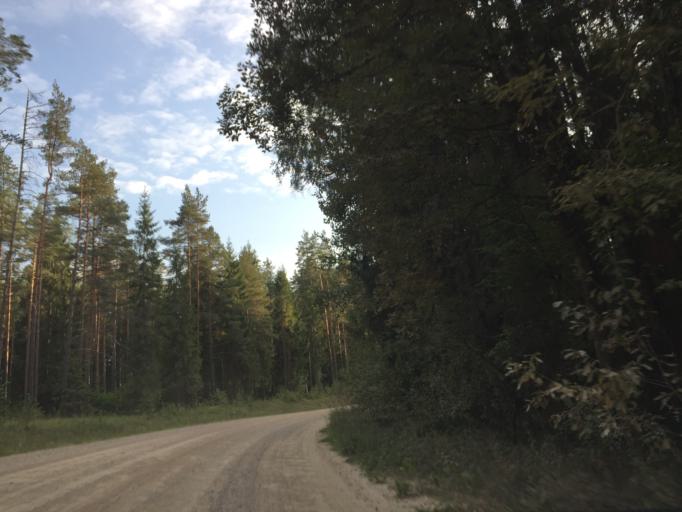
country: LV
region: Baldone
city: Baldone
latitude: 56.7875
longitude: 24.4433
